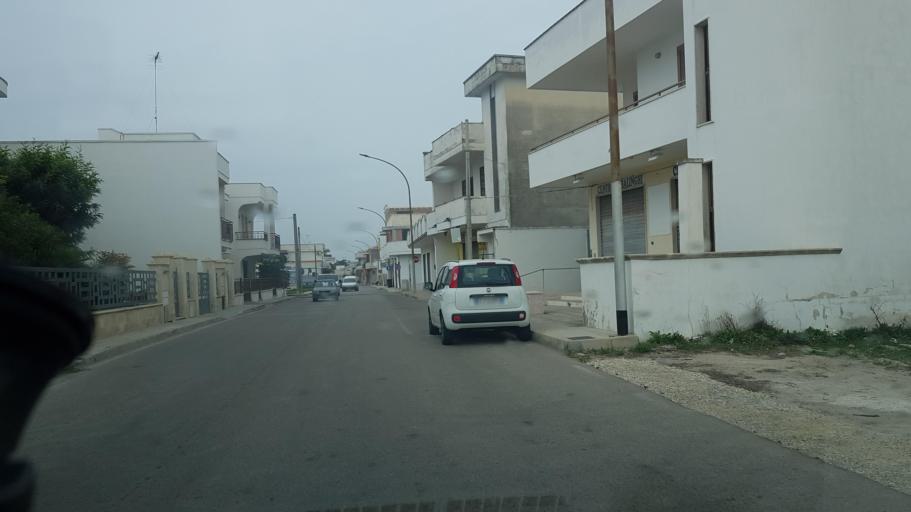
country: IT
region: Apulia
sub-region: Provincia di Lecce
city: Leverano
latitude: 40.2860
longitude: 17.9965
